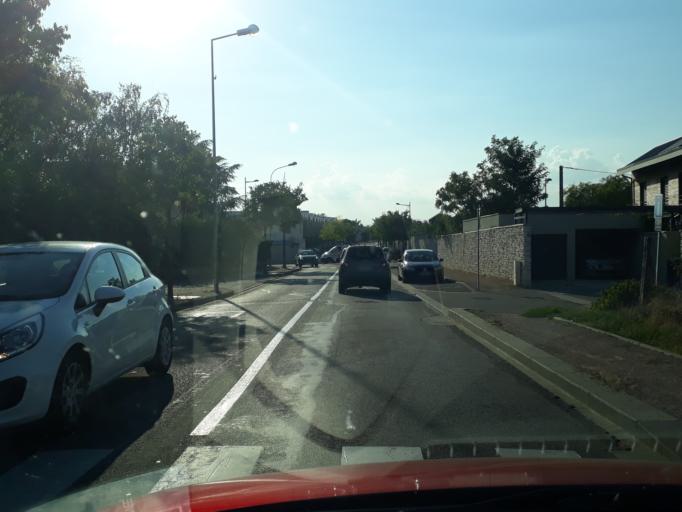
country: FR
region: Rhone-Alpes
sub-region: Departement du Rhone
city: Saint-Priest
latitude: 45.7066
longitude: 4.9412
